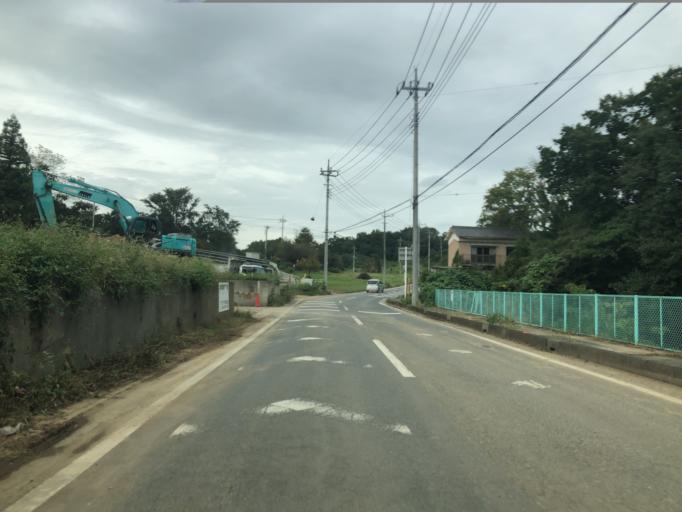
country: JP
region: Saitama
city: Kumagaya
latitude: 36.0661
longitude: 139.3879
